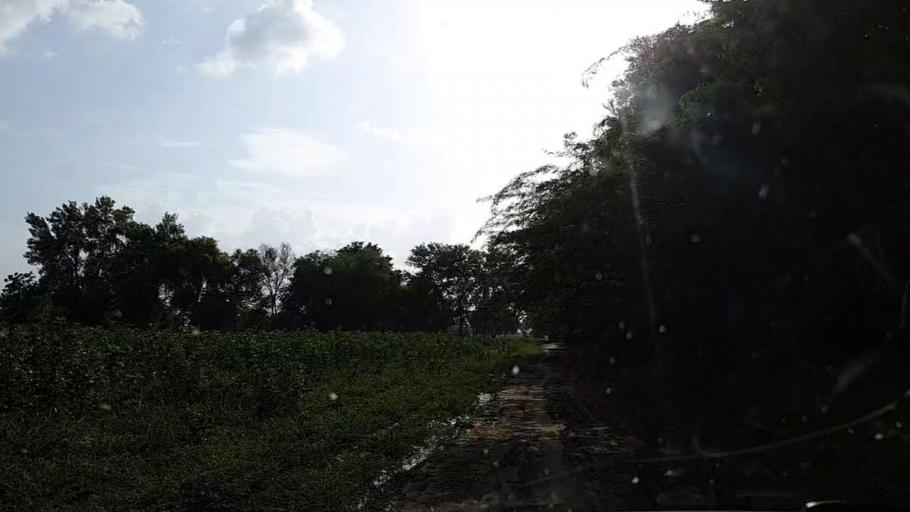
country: PK
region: Sindh
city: Bhiria
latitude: 26.8575
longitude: 68.2467
